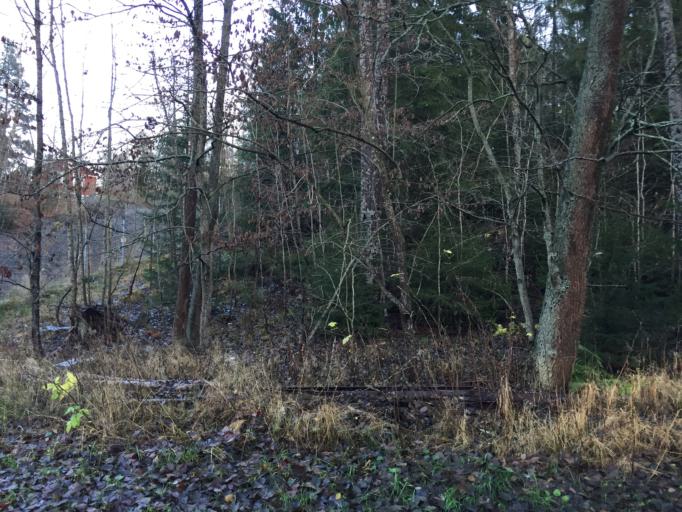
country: SE
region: Stockholm
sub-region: Salems Kommun
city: Ronninge
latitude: 59.1929
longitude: 17.7237
